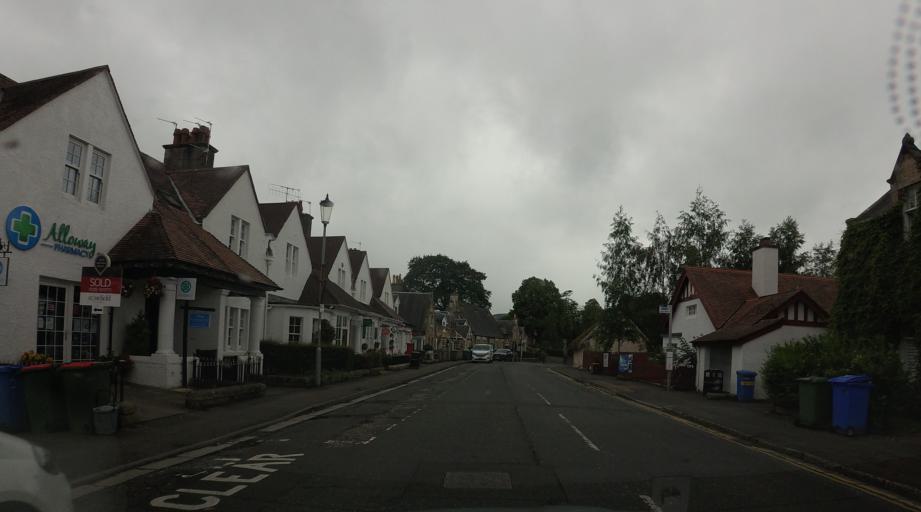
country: GB
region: Scotland
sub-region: South Ayrshire
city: Ayr
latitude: 55.4331
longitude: -4.6329
